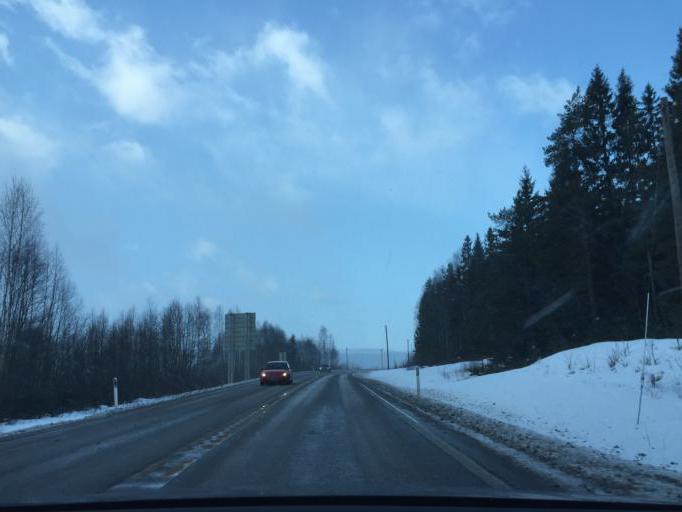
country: NO
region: Hedmark
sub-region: Sor-Odal
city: Skarnes
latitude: 60.2481
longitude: 11.7275
